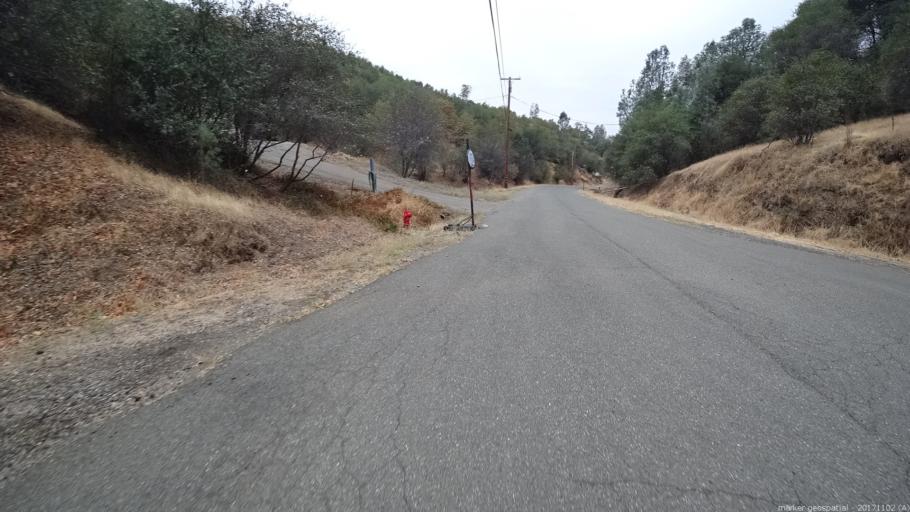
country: US
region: California
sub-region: Shasta County
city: Bella Vista
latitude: 40.7205
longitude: -122.2310
